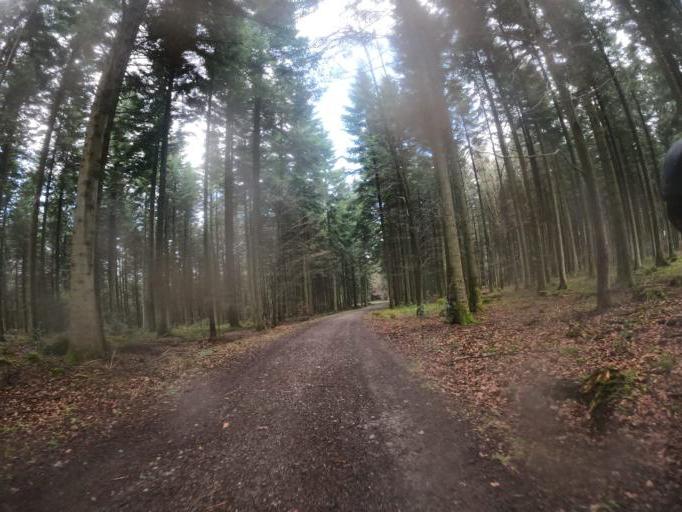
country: DE
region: Baden-Wuerttemberg
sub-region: Karlsruhe Region
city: Neuweiler
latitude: 48.6989
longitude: 8.5823
